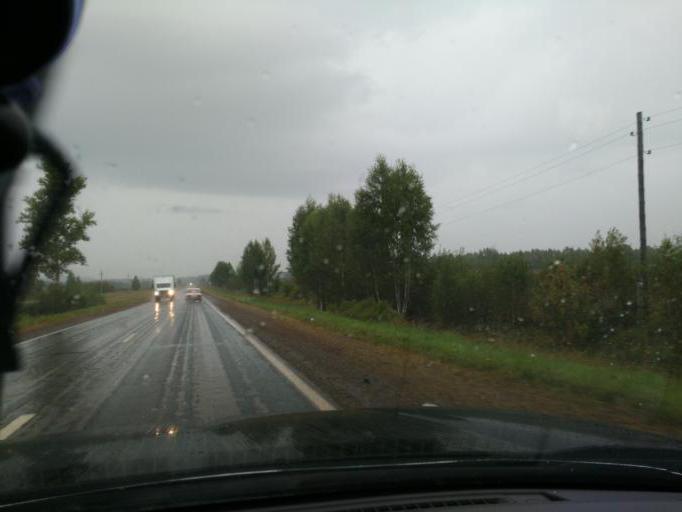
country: RU
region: Perm
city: Osa
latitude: 57.1349
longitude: 55.5267
